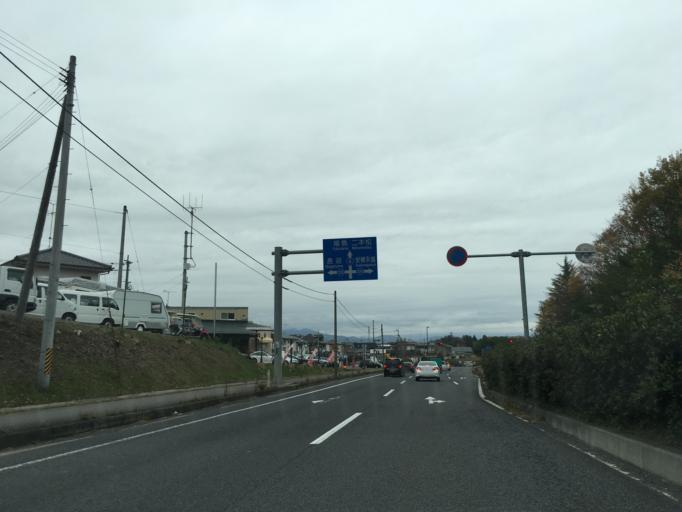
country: JP
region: Fukushima
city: Koriyama
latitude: 37.3433
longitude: 140.3586
